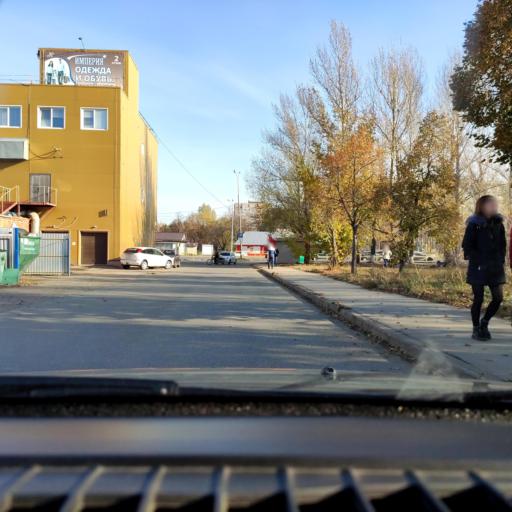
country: RU
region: Samara
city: Tol'yatti
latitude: 53.5333
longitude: 49.2811
